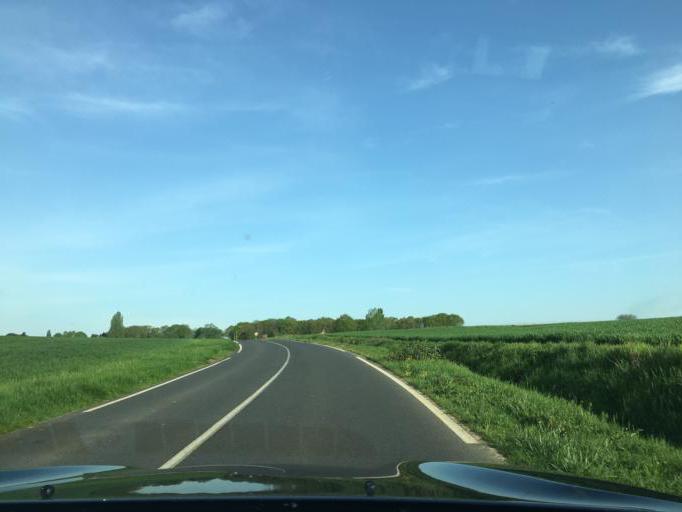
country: FR
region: Centre
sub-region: Departement d'Eure-et-Loir
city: Epernon
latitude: 48.6519
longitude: 1.6853
